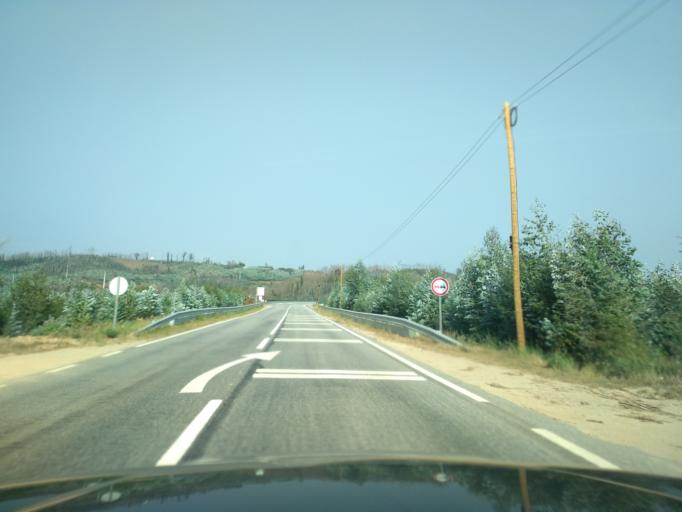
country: PT
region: Viseu
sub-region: Santa Comba Dao
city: Santa Comba Dao
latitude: 40.3922
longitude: -8.1674
